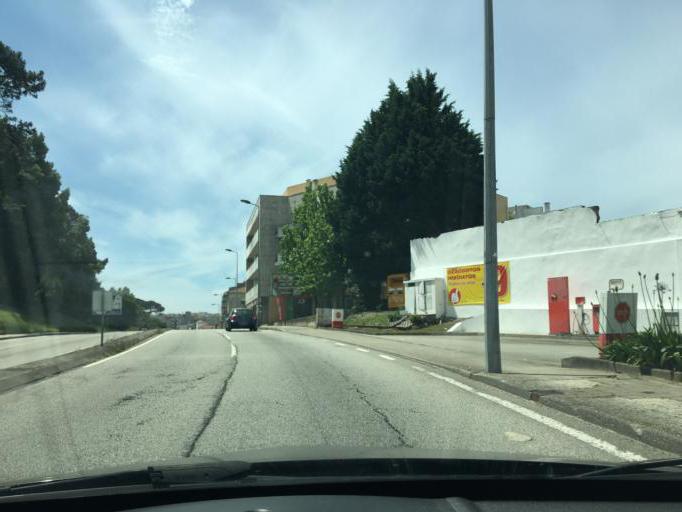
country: PT
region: Porto
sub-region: Porto
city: Porto
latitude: 41.1690
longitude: -8.6065
